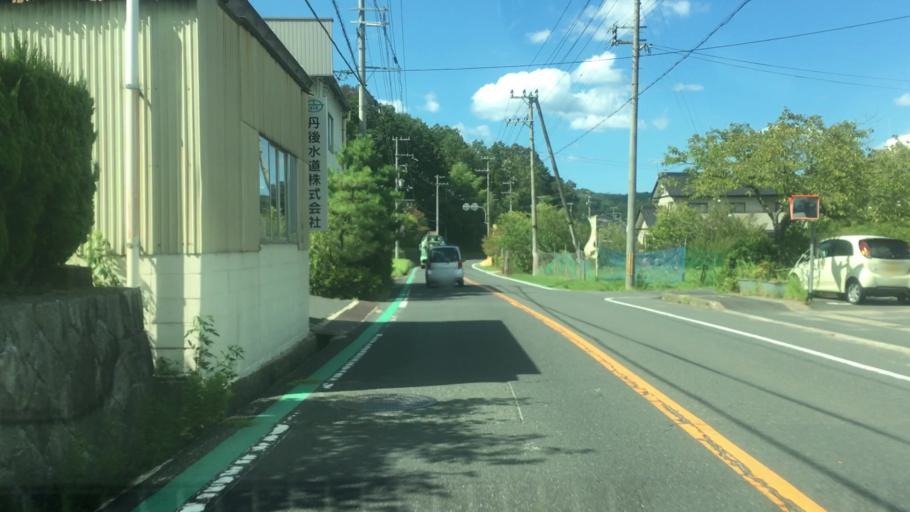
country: JP
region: Kyoto
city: Miyazu
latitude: 35.6160
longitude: 135.0537
